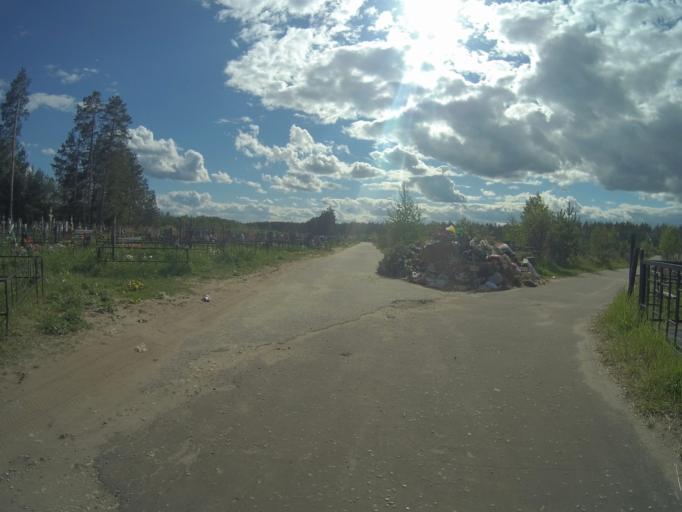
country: RU
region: Vladimir
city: Golovino
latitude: 56.0290
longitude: 40.4256
